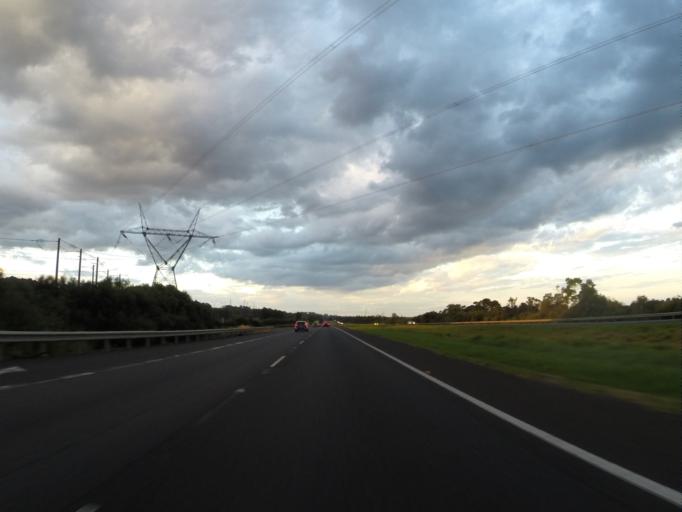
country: AU
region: New South Wales
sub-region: Campbelltown Municipality
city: Glen Alpine
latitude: -34.0854
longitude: 150.7697
